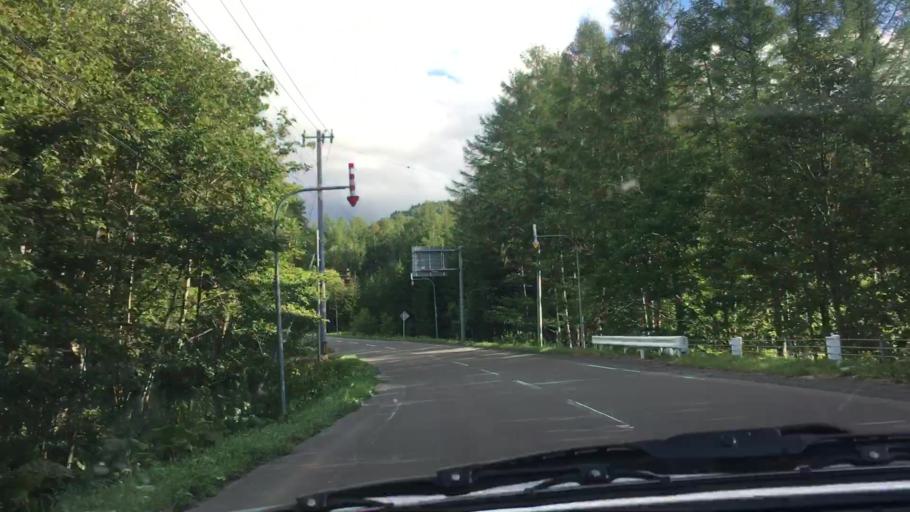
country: JP
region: Hokkaido
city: Shimo-furano
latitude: 43.1208
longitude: 142.6806
